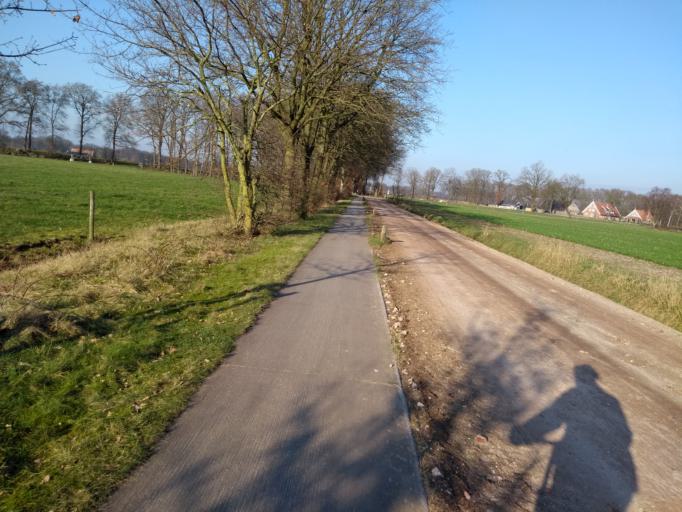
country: NL
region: Overijssel
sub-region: Gemeente Tubbergen
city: Tubbergen
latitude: 52.3967
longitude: 6.7384
